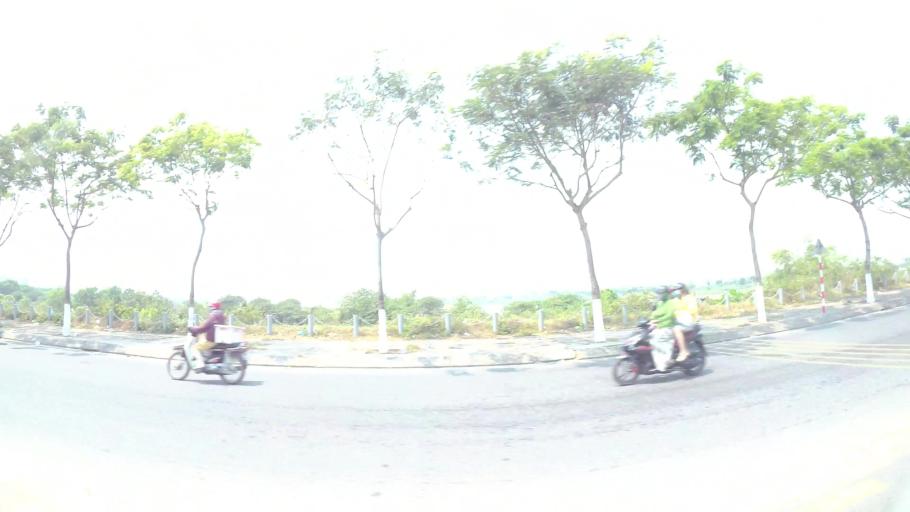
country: VN
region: Da Nang
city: Cam Le
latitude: 16.0067
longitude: 108.2079
